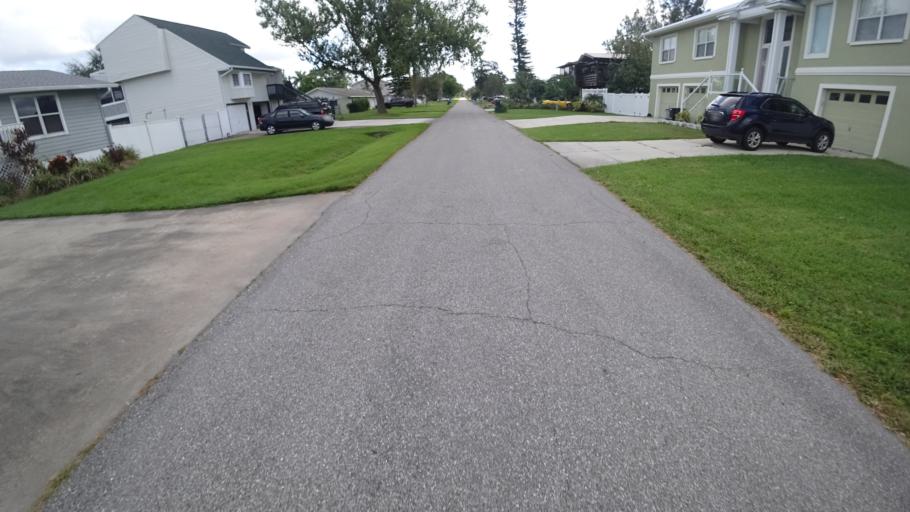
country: US
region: Florida
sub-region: Manatee County
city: Memphis
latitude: 27.5561
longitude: -82.5710
